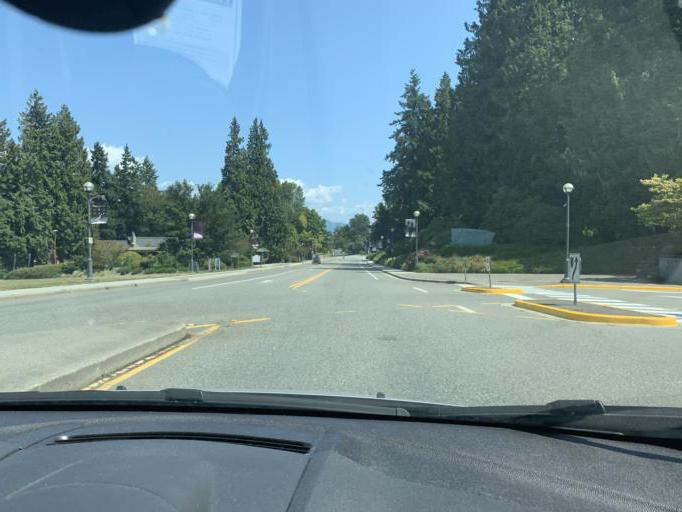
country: CA
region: British Columbia
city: West End
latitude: 49.2697
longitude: -123.2568
